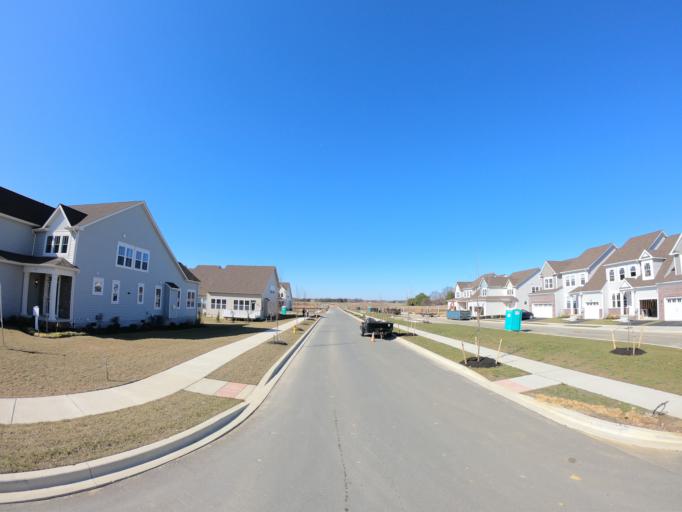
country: US
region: Delaware
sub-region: New Castle County
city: Middletown
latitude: 39.4983
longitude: -75.6690
